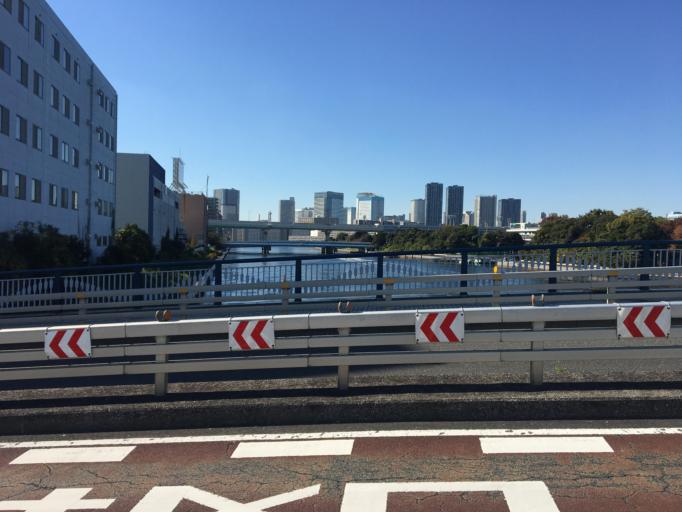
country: JP
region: Tokyo
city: Urayasu
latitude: 35.6542
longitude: 139.8158
